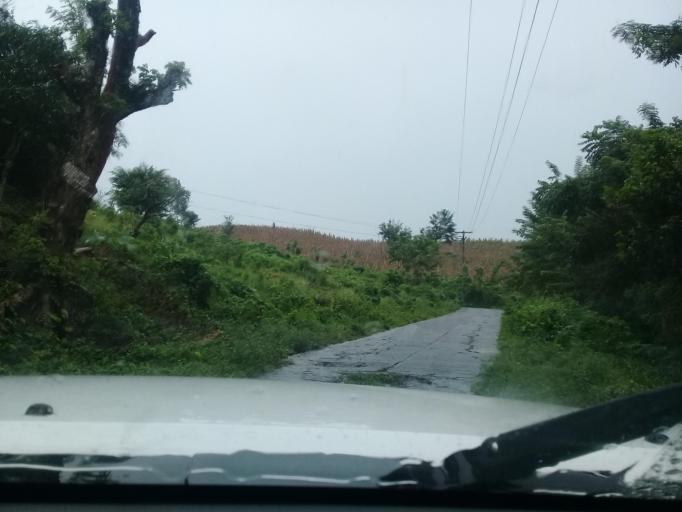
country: MX
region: Veracruz
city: Santiago Tuxtla
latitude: 18.4608
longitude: -95.3200
